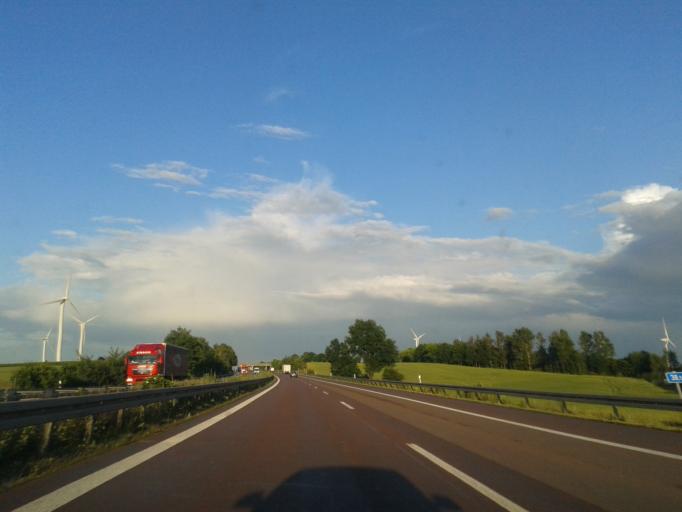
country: DE
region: Saxony
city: Ostrau
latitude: 51.2225
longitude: 12.9131
